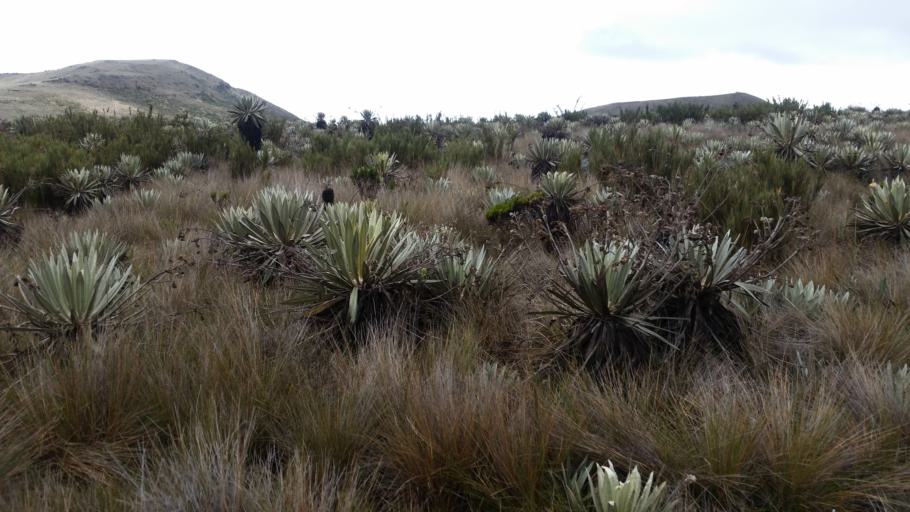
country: CO
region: Cundinamarca
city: Pasca
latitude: 4.3694
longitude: -74.2175
